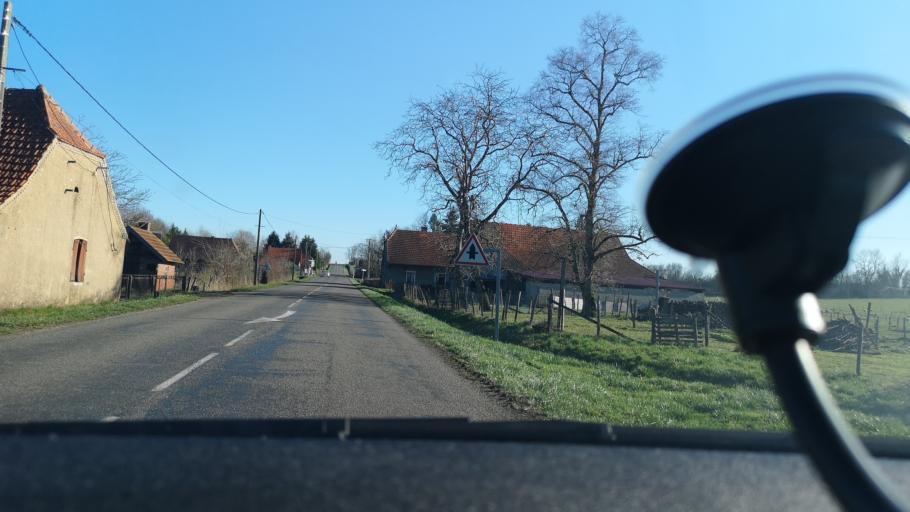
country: FR
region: Bourgogne
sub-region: Departement de Saone-et-Loire
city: Saint-Germain-du-Bois
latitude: 46.7485
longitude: 5.2985
